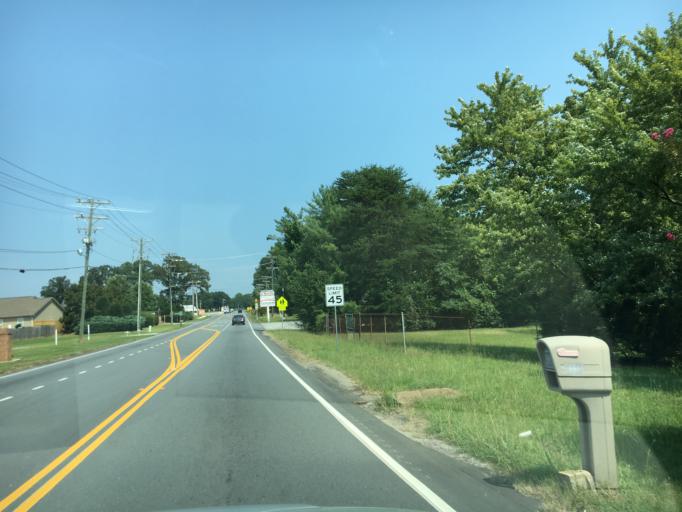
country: US
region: South Carolina
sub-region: Spartanburg County
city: Valley Falls
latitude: 35.0236
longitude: -81.9500
